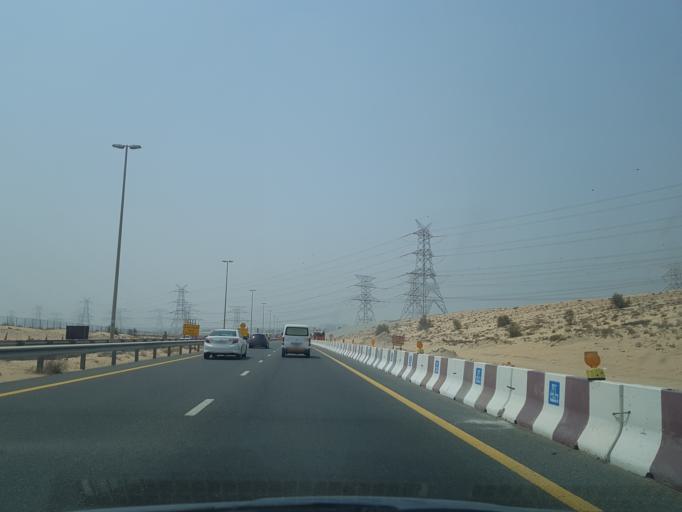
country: AE
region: Ash Shariqah
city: Sharjah
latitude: 25.1434
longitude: 55.4230
